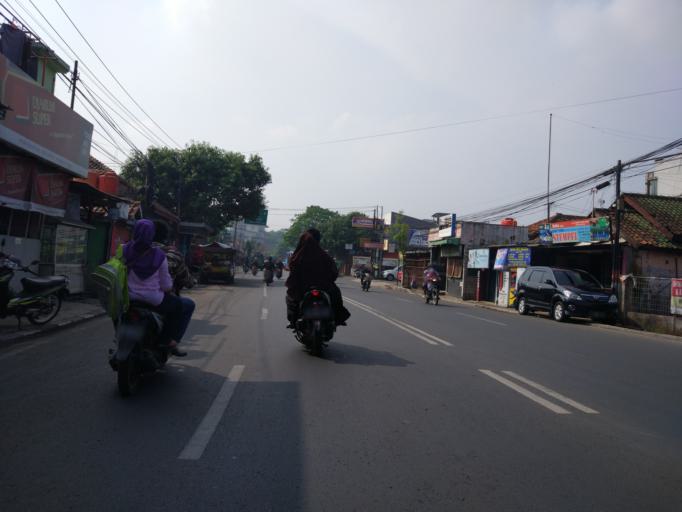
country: ID
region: West Java
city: Cileunyi
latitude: -6.9316
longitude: 107.7135
